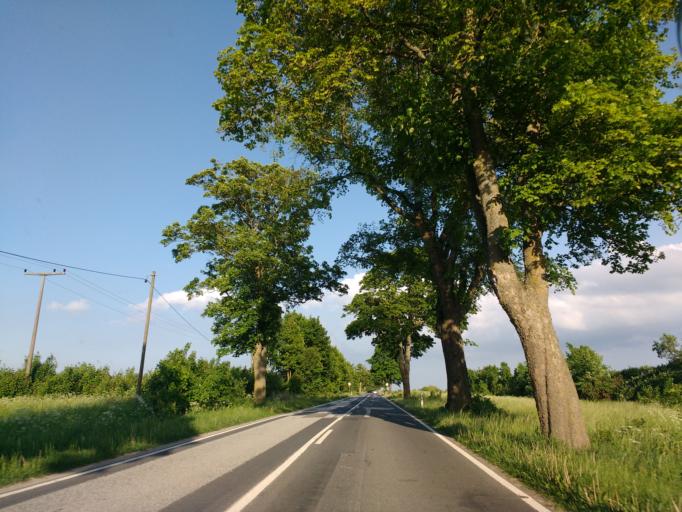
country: DE
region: Mecklenburg-Vorpommern
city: Sellin
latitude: 53.8757
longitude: 11.5816
